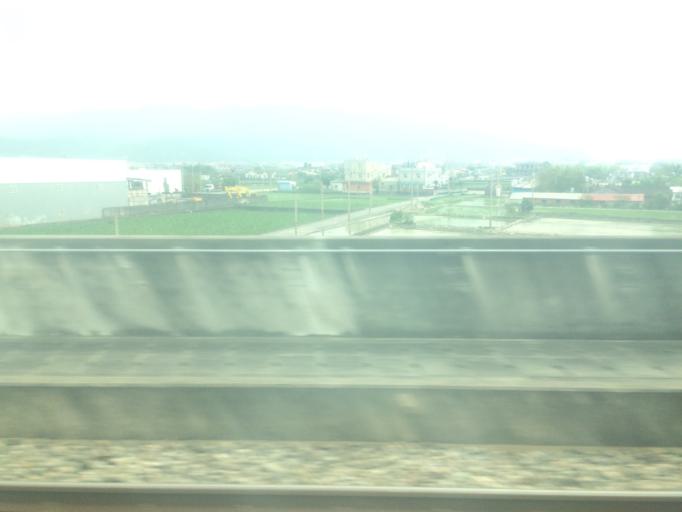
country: TW
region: Taiwan
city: Fengyuan
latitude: 24.3793
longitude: 120.6839
